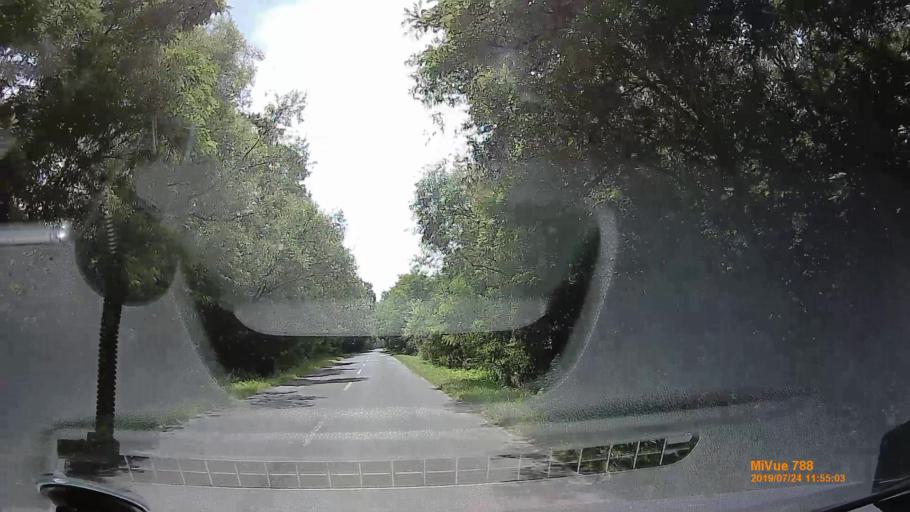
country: HU
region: Szabolcs-Szatmar-Bereg
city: Vasarosnameny
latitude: 48.2132
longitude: 22.4126
